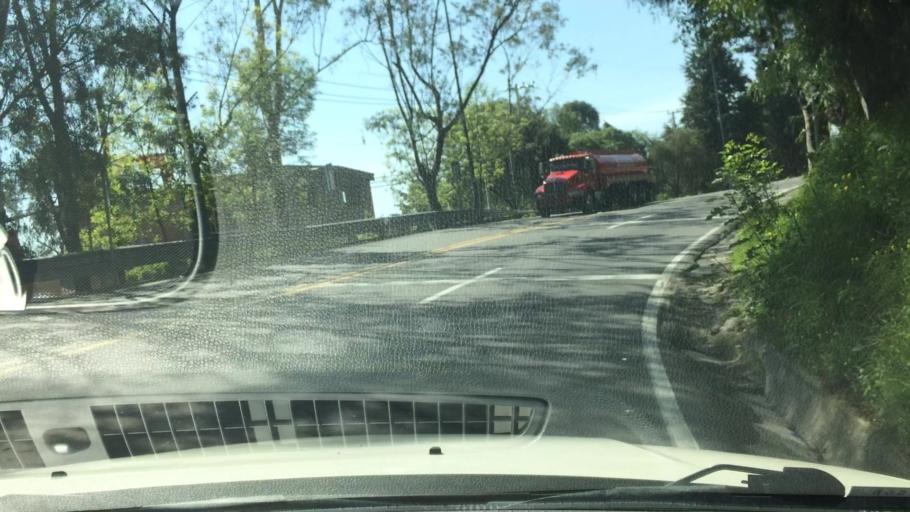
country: MX
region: Mexico City
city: Tlalpan
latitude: 19.2405
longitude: -99.1612
